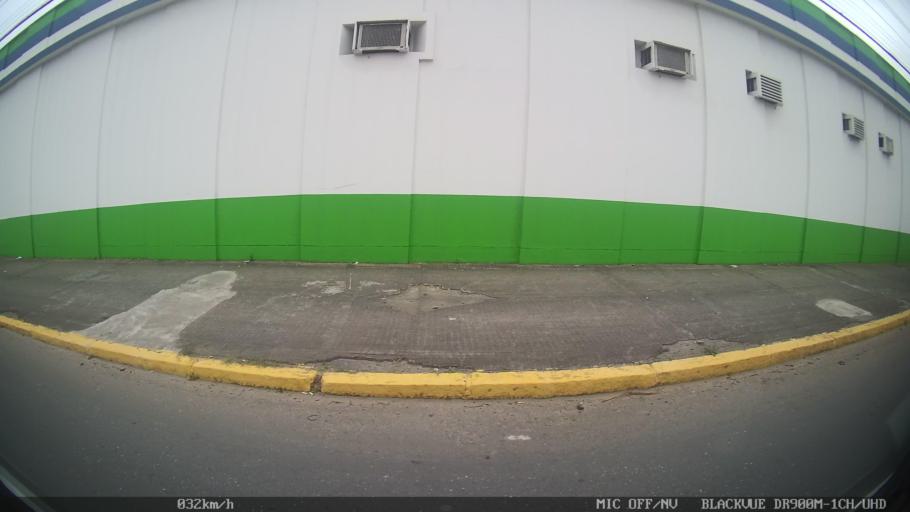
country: BR
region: Santa Catarina
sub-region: Joinville
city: Joinville
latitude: -26.3221
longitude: -48.8449
